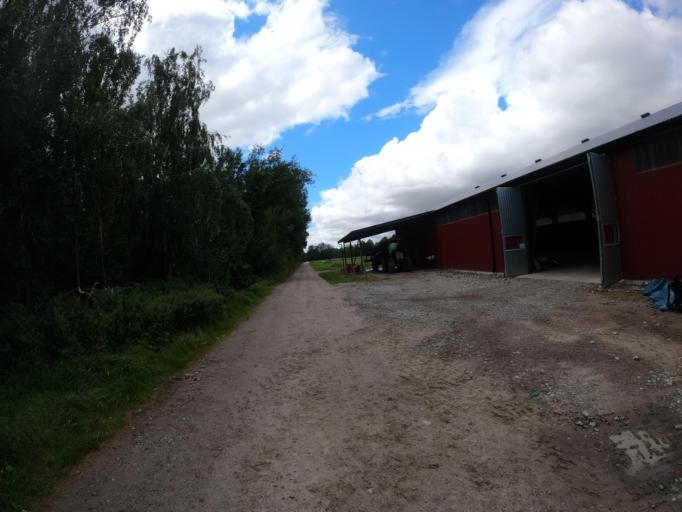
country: SE
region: Skane
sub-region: Hoors Kommun
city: Loberod
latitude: 55.7325
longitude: 13.4189
